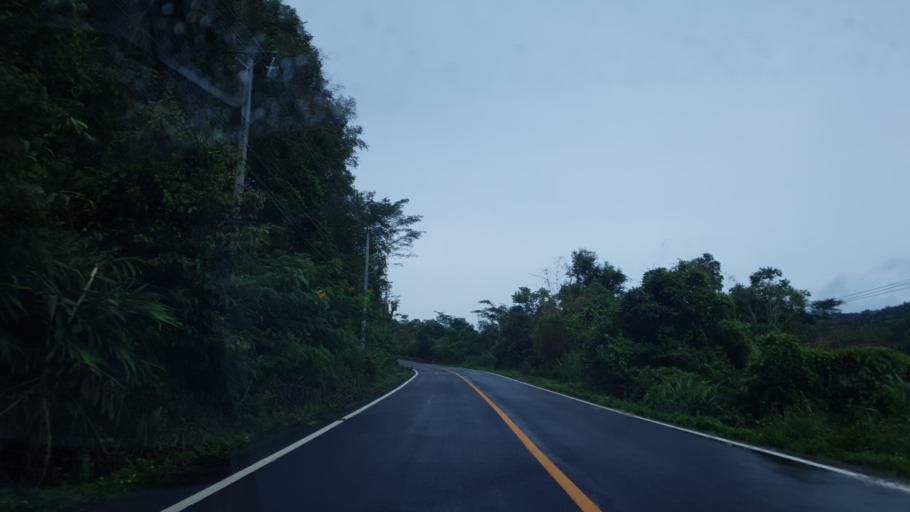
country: TH
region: Mae Hong Son
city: Ban Huai I Huak
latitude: 18.1429
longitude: 98.1041
